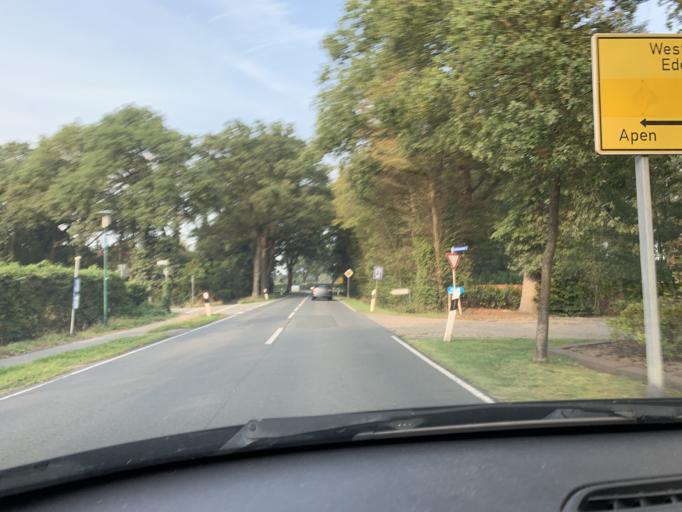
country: DE
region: Lower Saxony
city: Apen
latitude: 53.1776
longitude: 7.7780
